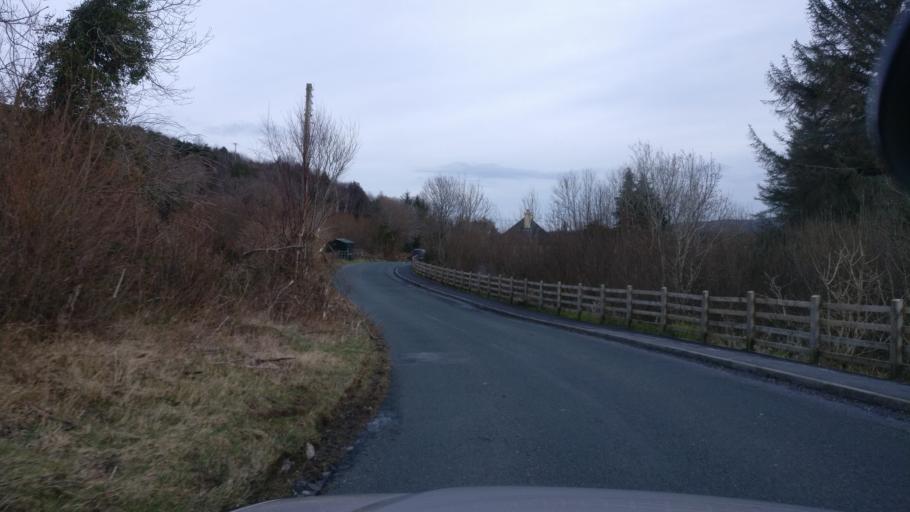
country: IE
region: Connaught
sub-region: County Galway
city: Oughterard
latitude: 53.5200
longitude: -9.4562
